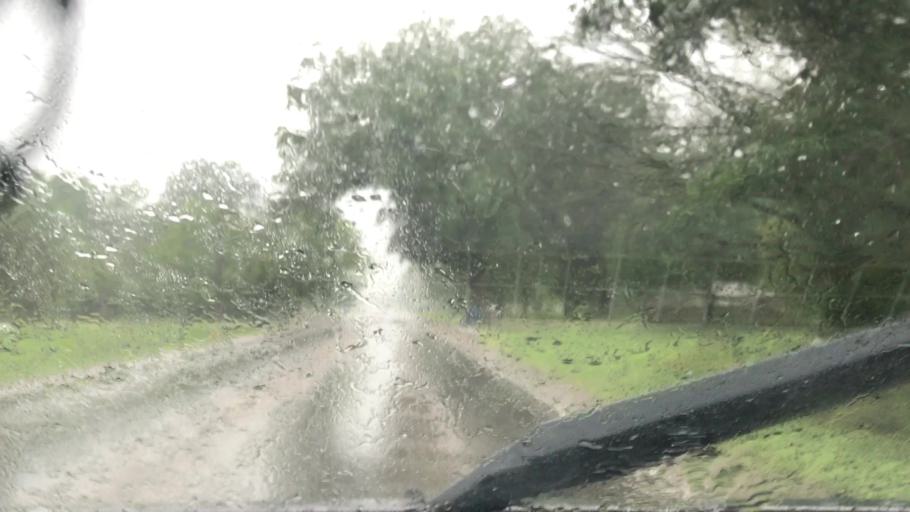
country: US
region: Indiana
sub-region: Hamilton County
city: Sheridan
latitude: 40.1249
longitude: -86.1984
